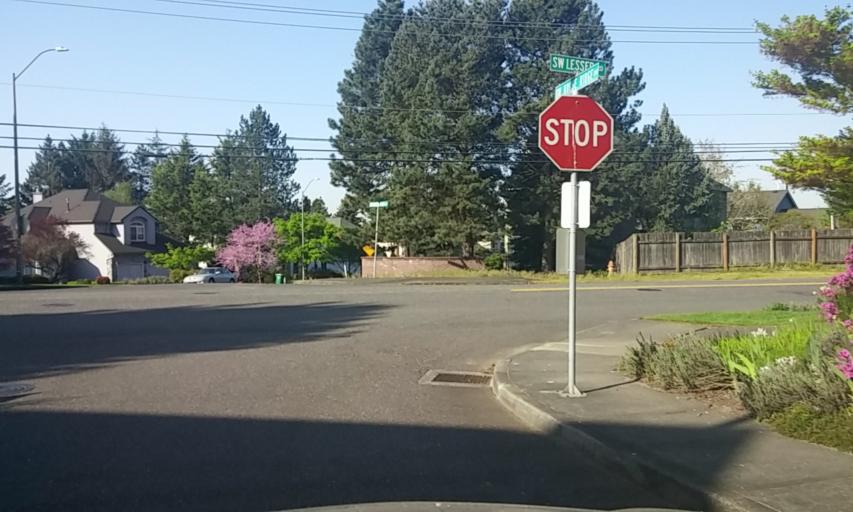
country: US
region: Oregon
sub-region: Washington County
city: Metzger
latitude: 45.4340
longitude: -122.7362
